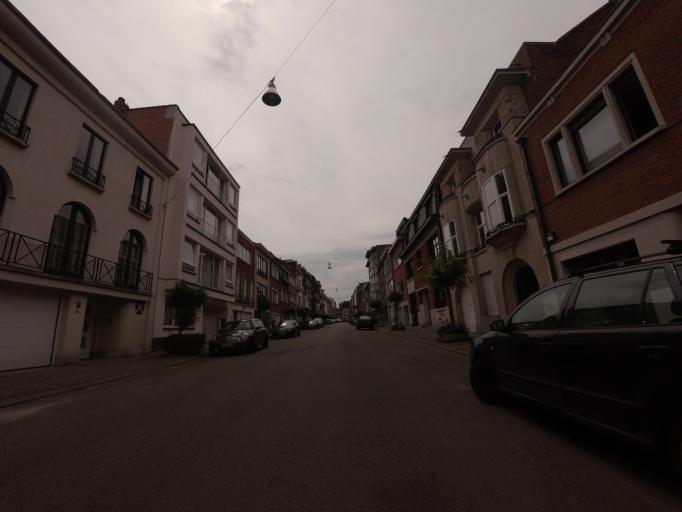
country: BE
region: Brussels Capital
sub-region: Bruxelles-Capitale
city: Brussels
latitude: 50.8156
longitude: 4.3632
